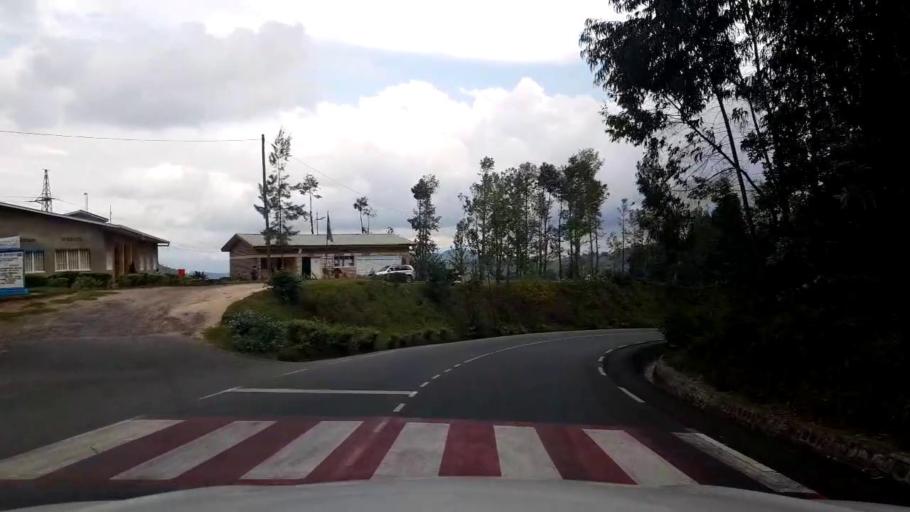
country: RW
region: Northern Province
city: Musanze
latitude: -1.6742
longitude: 29.5166
